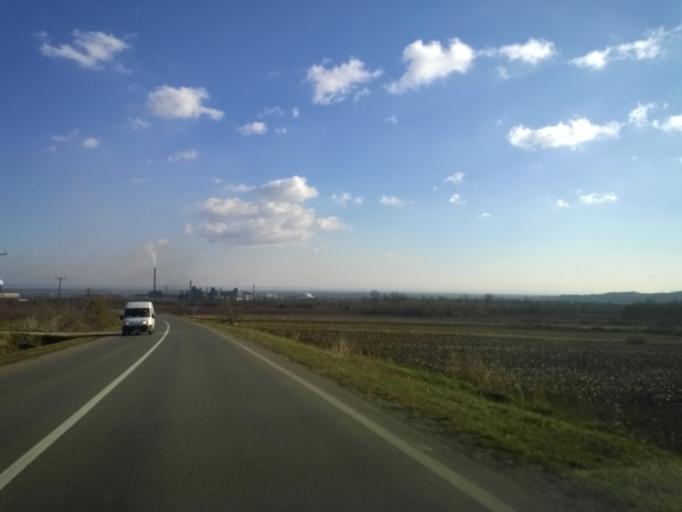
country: RS
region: Central Serbia
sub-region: Podunavski Okrug
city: Smederevo
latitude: 44.6095
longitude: 20.9393
